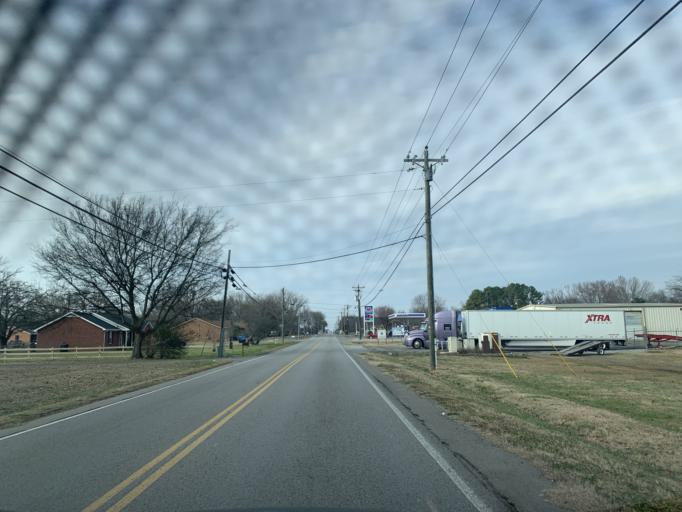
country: US
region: Tennessee
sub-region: Rutherford County
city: Smyrna
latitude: 35.9321
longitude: -86.4903
